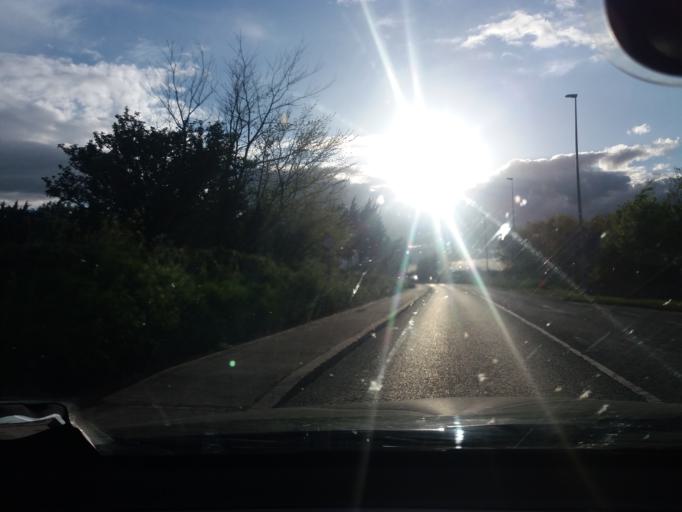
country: IE
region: Leinster
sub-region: South Dublin
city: Rathcoole
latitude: 53.2940
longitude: -6.4815
